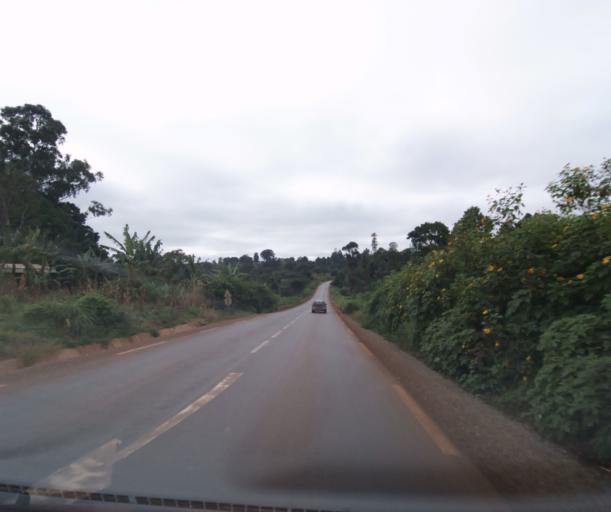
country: CM
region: West
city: Mbouda
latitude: 5.5755
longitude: 10.3068
